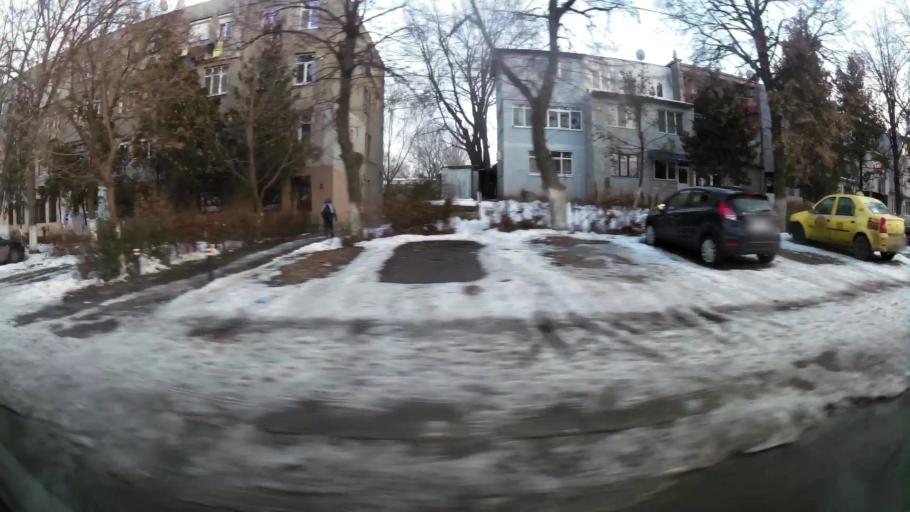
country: RO
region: Ilfov
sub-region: Comuna Popesti-Leordeni
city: Popesti-Leordeni
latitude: 44.3658
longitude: 26.1948
